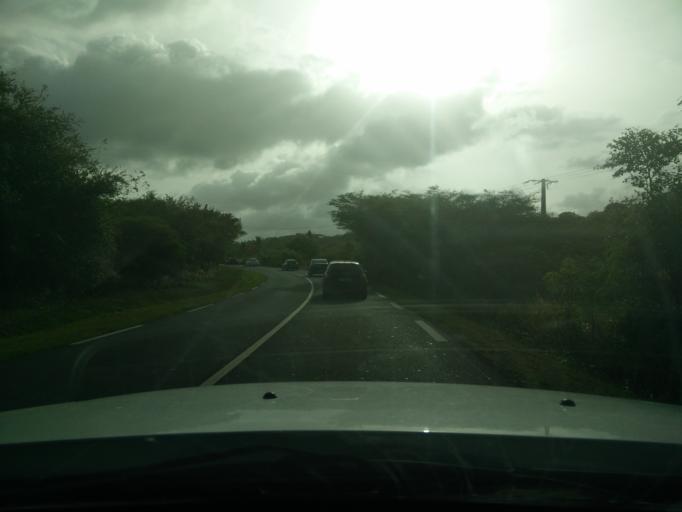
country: GP
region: Guadeloupe
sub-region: Guadeloupe
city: Saint-Francois
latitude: 16.2585
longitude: -61.3030
